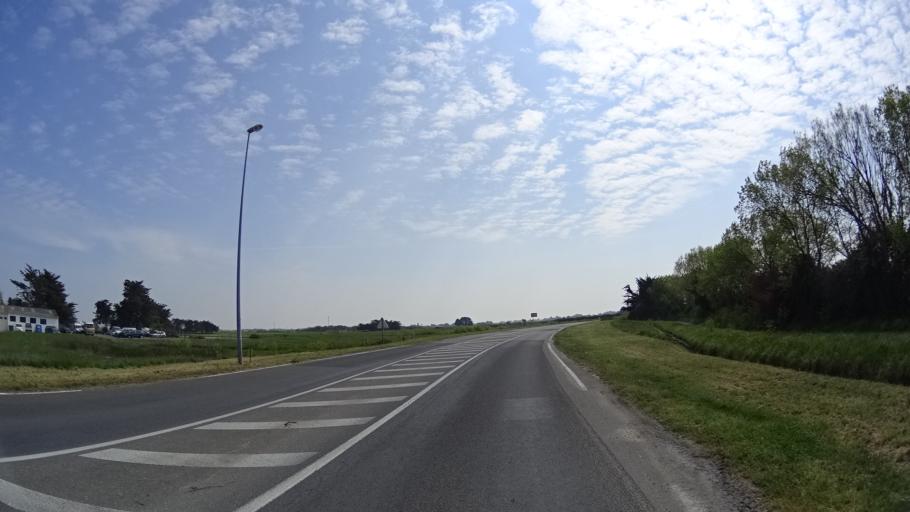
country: FR
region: Pays de la Loire
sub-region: Departement de la Vendee
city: La Gueriniere
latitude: 46.9817
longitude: -2.2634
